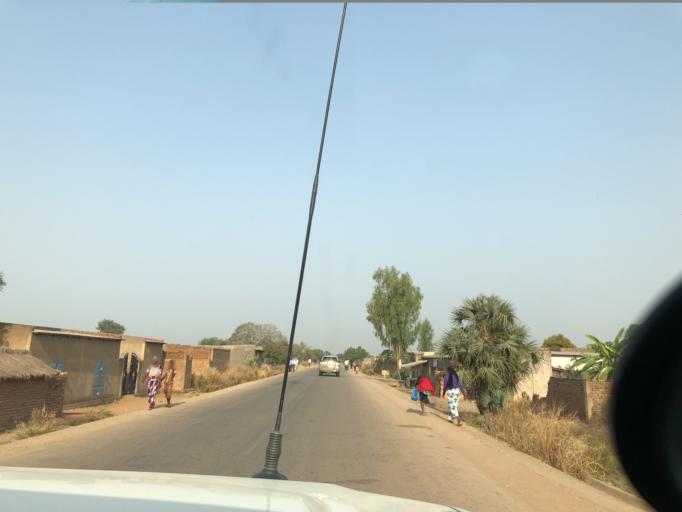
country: TD
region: Logone Occidental
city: Moundou
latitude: 8.5674
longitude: 16.0510
